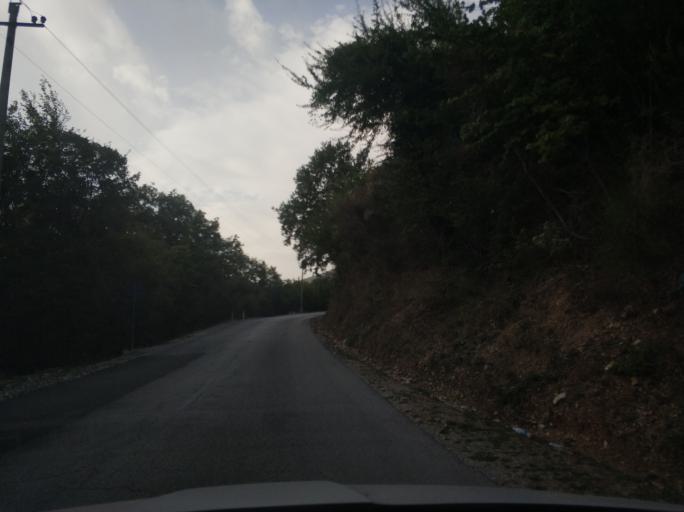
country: AL
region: Vlore
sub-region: Rrethi i Sarandes
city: Dhiver
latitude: 39.9193
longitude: 20.2008
